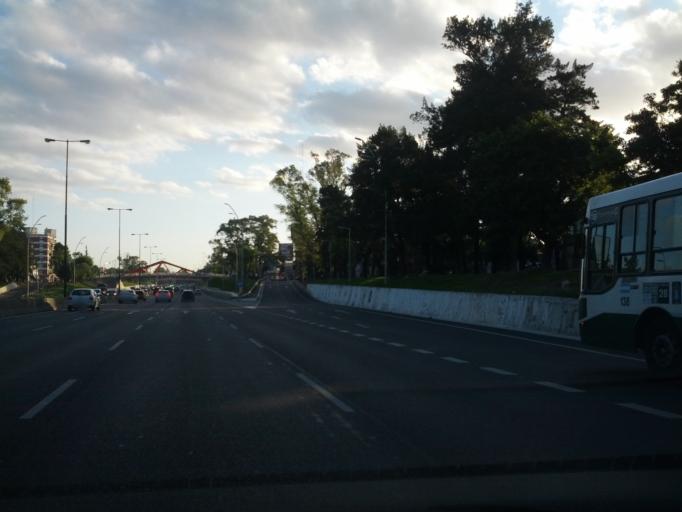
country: AR
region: Buenos Aires
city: Caseros
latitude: -34.6088
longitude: -58.5279
